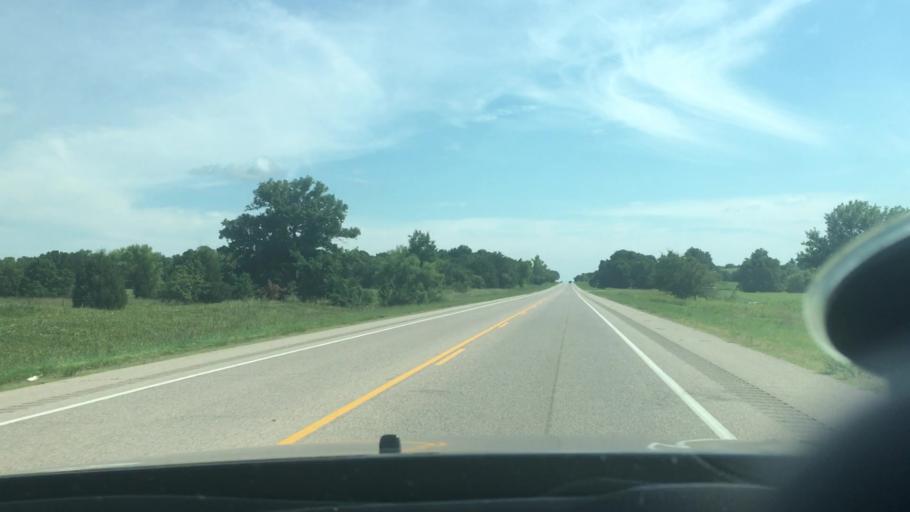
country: US
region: Oklahoma
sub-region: Seminole County
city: Seminole
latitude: 35.1695
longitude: -96.6742
